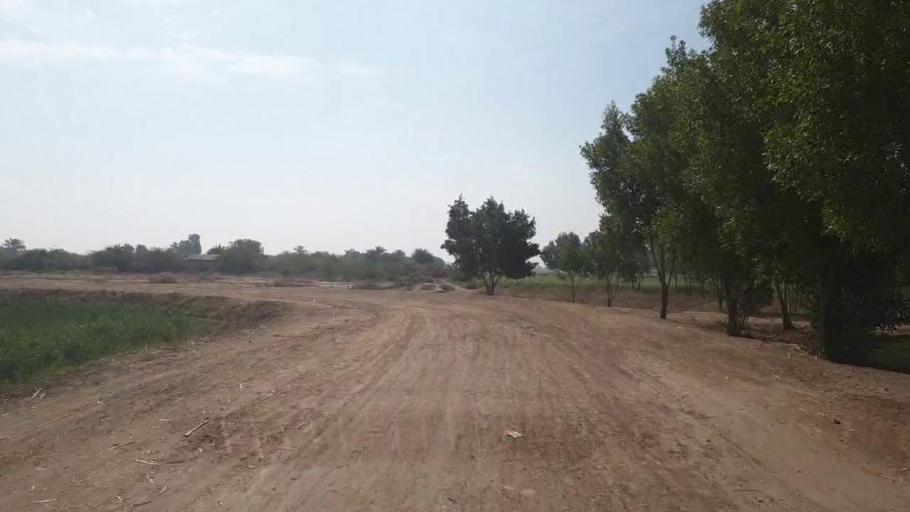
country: PK
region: Sindh
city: Mirwah Gorchani
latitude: 25.3703
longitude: 69.2036
